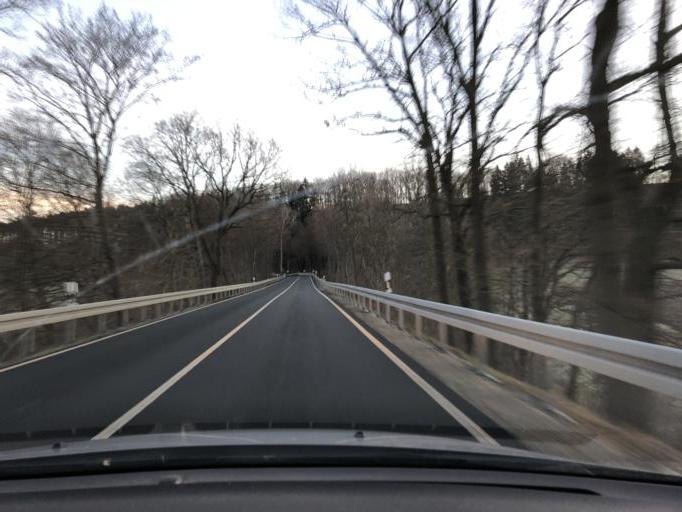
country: DE
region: Thuringia
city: Schwarza
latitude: 50.8484
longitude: 11.3367
